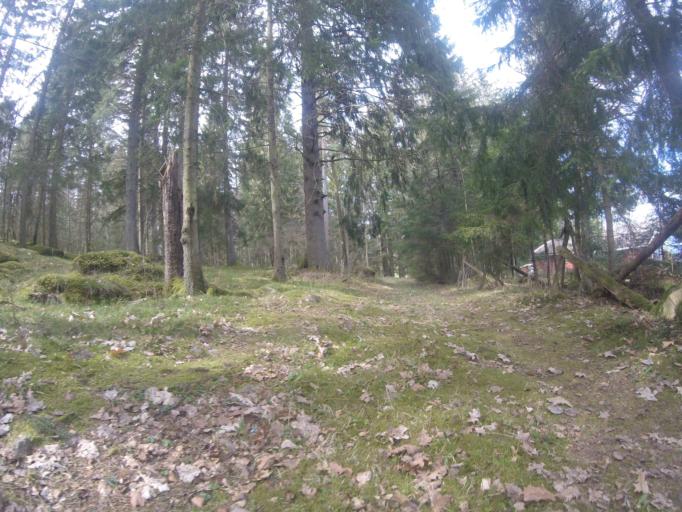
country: SE
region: Vaestra Goetaland
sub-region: Alingsas Kommun
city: Ingared
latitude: 57.8709
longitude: 12.5146
